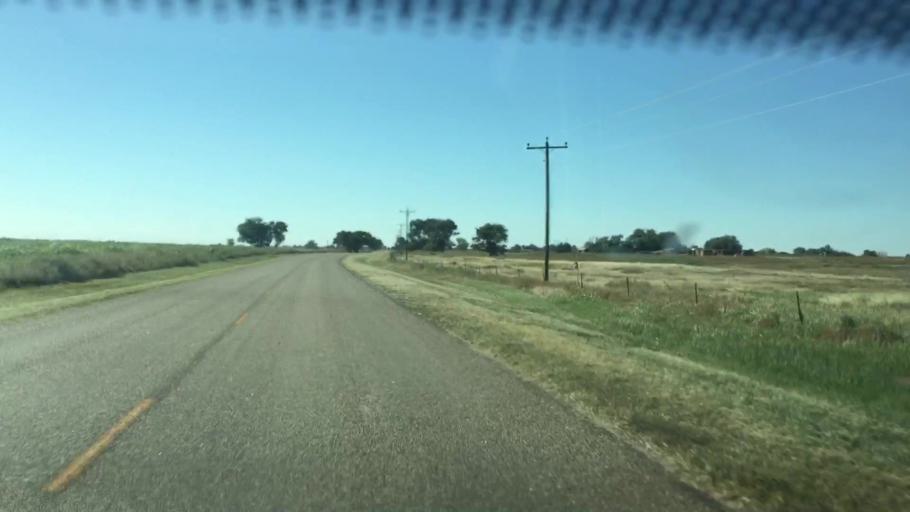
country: US
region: Colorado
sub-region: Prowers County
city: Lamar
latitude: 38.1146
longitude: -102.5781
